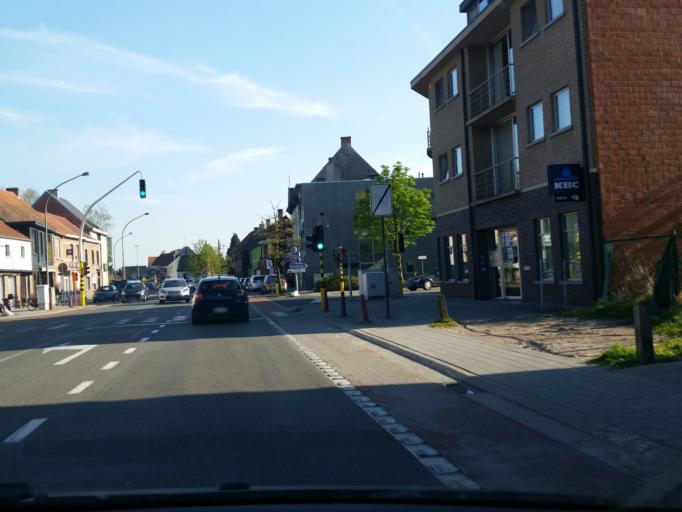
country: BE
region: Flanders
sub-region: Provincie Oost-Vlaanderen
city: Stekene
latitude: 51.2064
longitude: 4.0756
